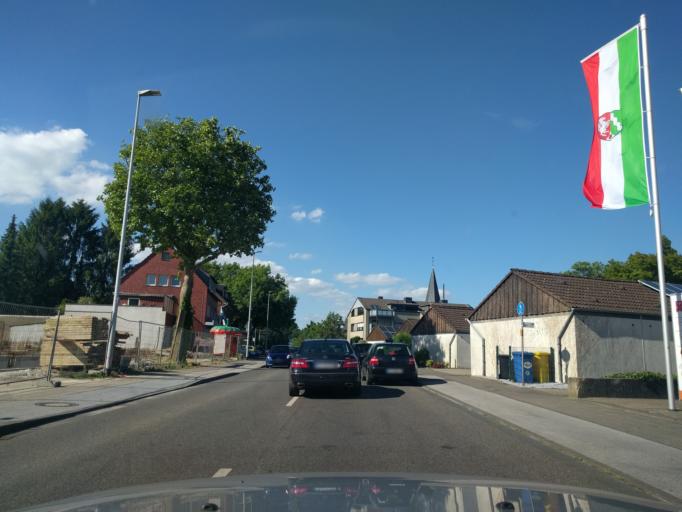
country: DE
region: North Rhine-Westphalia
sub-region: Regierungsbezirk Dusseldorf
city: Kaarst
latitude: 51.2329
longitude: 6.6154
